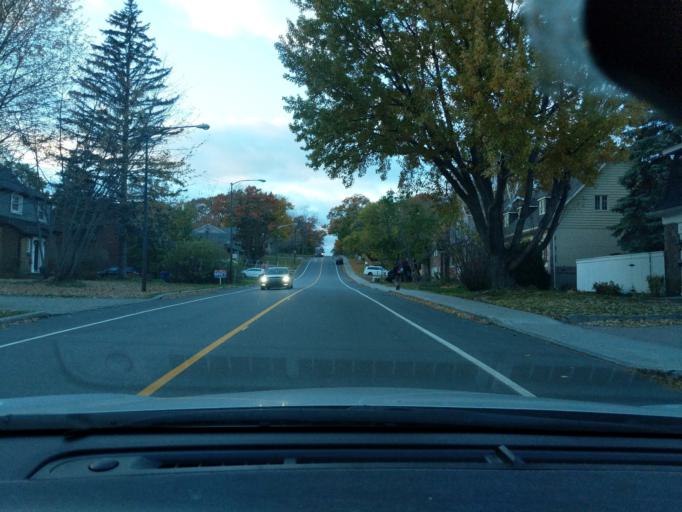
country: CA
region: Quebec
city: Quebec
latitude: 46.7695
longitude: -71.2669
